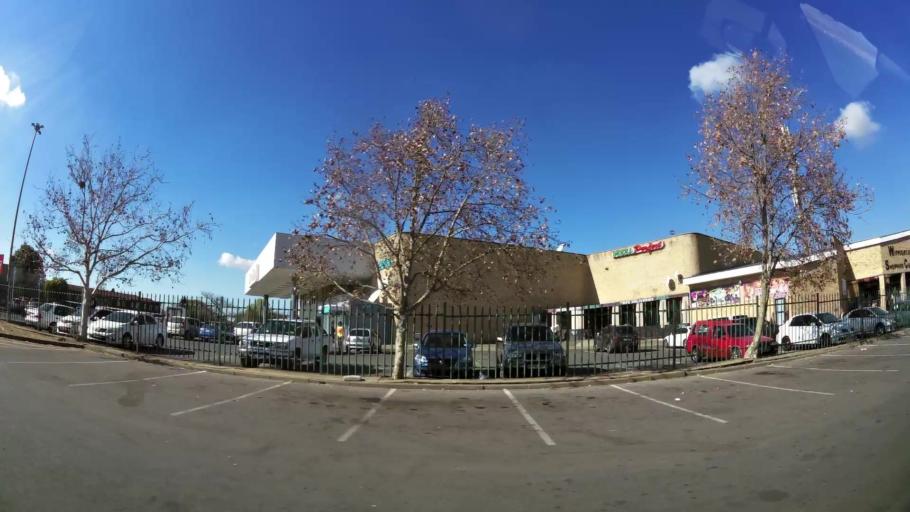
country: ZA
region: Gauteng
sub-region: City of Johannesburg Metropolitan Municipality
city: Roodepoort
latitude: -26.1405
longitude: 27.8313
